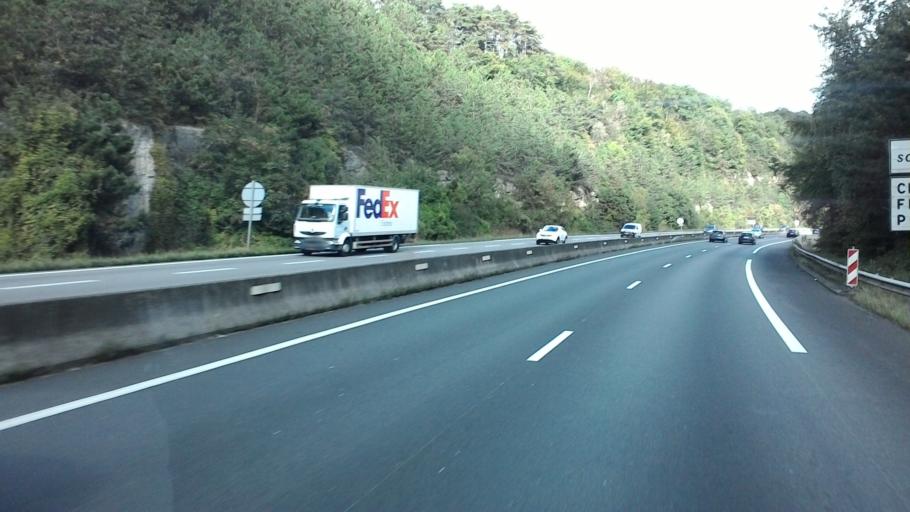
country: FR
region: Lorraine
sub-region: Departement de Meurthe-et-Moselle
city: Maxeville
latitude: 48.7126
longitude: 6.1487
